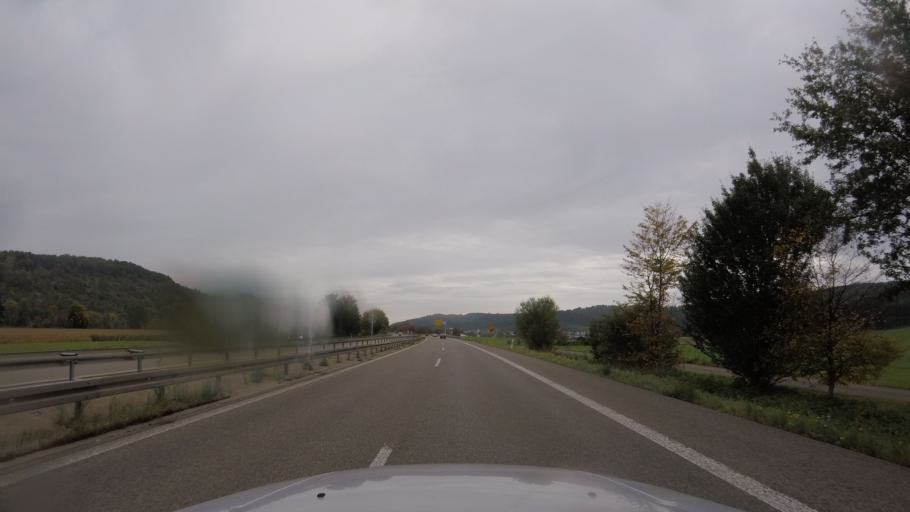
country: DE
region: Baden-Wuerttemberg
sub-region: Regierungsbezirk Stuttgart
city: Pluderhausen
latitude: 48.7836
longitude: 9.6172
